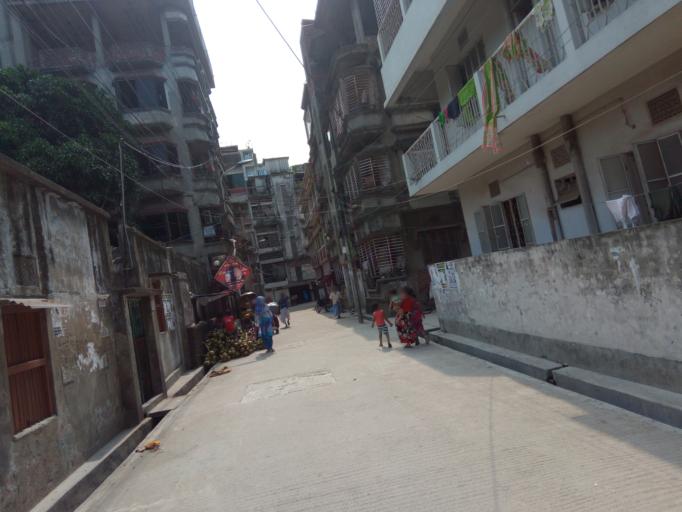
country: BD
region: Dhaka
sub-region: Dhaka
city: Dhaka
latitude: 23.6998
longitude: 90.4282
